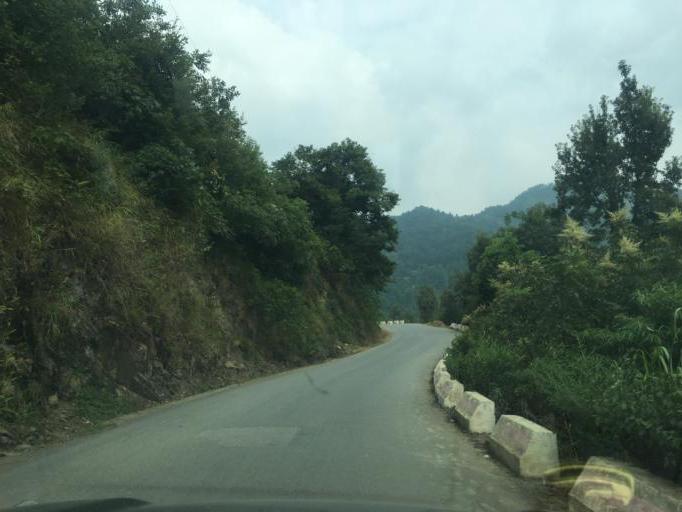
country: CN
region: Guangxi Zhuangzu Zizhiqu
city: Tongle
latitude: 25.3304
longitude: 106.0127
